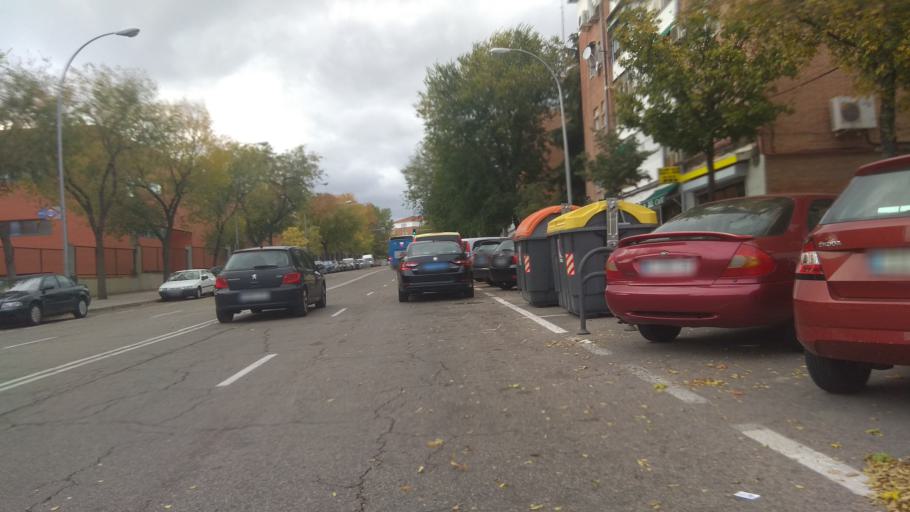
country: ES
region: Madrid
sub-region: Provincia de Madrid
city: Vicalvaro
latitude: 40.4076
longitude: -3.6092
